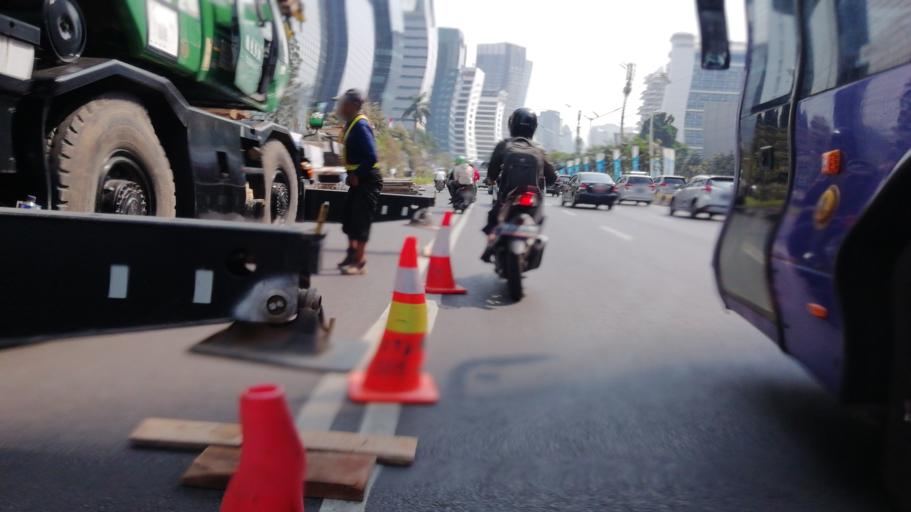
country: ID
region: Jakarta Raya
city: Jakarta
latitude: -6.2102
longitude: 106.8214
